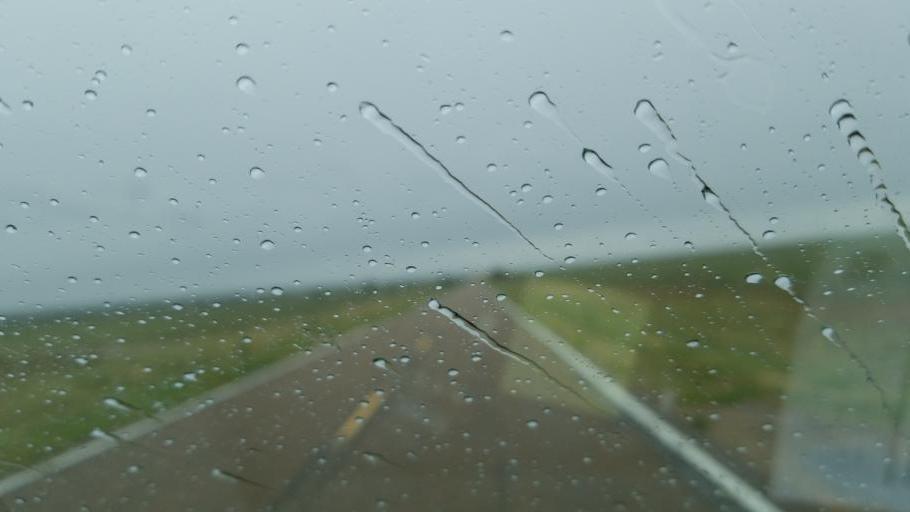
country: US
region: Colorado
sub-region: Lincoln County
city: Hugo
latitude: 38.8636
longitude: -103.1358
